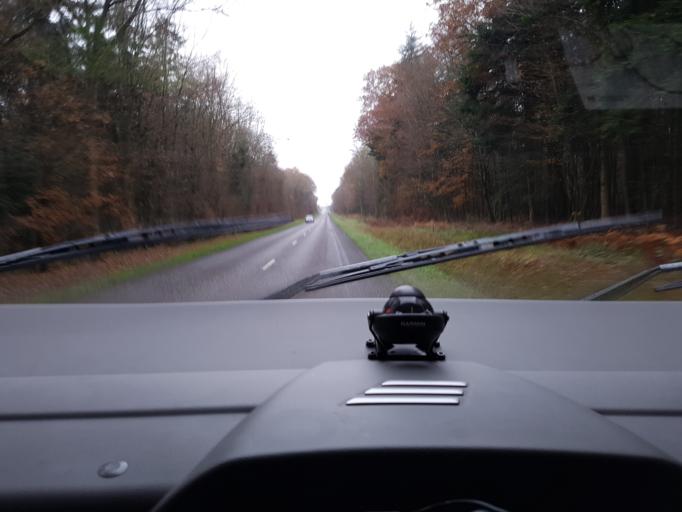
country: FR
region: Haute-Normandie
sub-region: Departement de l'Eure
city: Rugles
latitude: 48.8540
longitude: 0.7344
